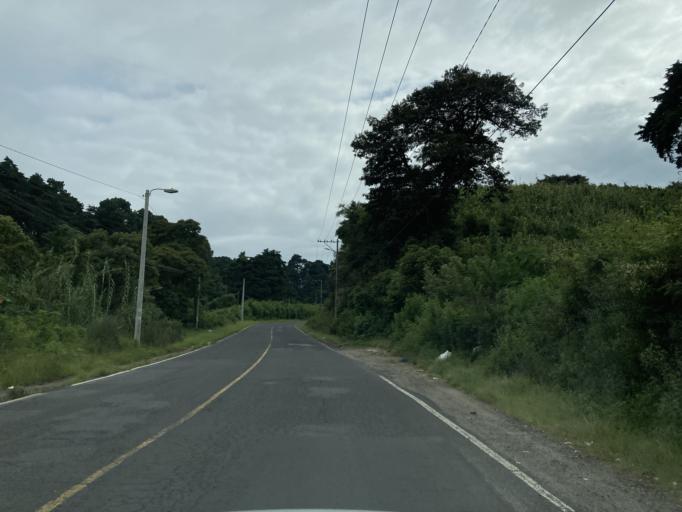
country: GT
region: Guatemala
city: San Jose Pinula
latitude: 14.5320
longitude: -90.4098
